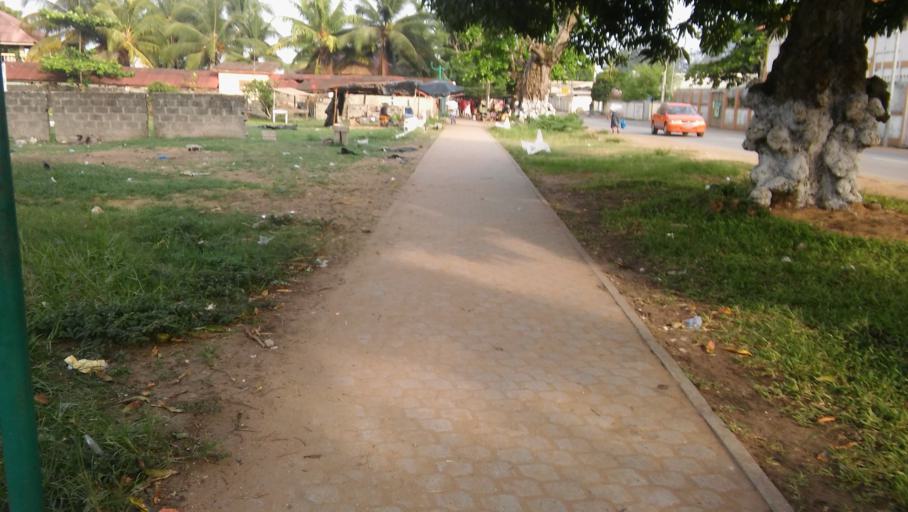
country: CI
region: Sud-Comoe
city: Grand-Bassam
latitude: 5.1974
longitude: -3.7353
